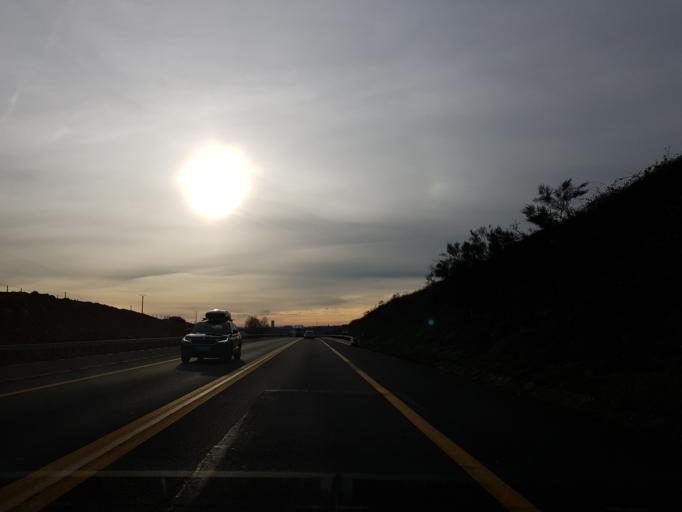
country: FR
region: Auvergne
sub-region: Departement de l'Allier
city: Montmarault
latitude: 46.3475
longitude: 2.9930
